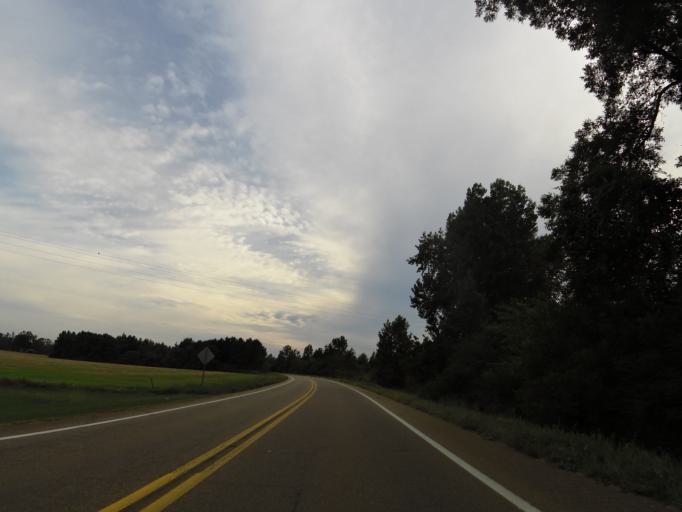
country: US
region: Alabama
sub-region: Monroe County
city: Frisco City
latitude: 31.4174
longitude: -87.4260
